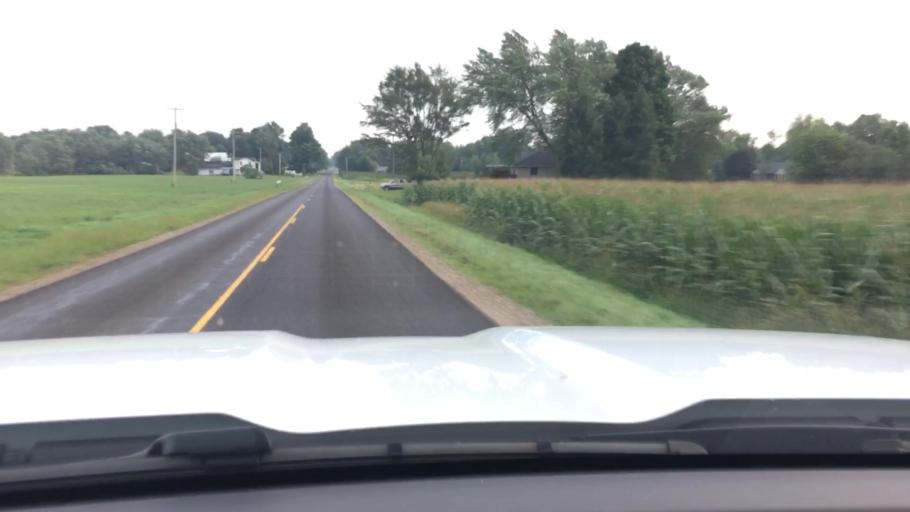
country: US
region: Michigan
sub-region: Ottawa County
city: Hudsonville
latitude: 42.8014
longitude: -85.8814
